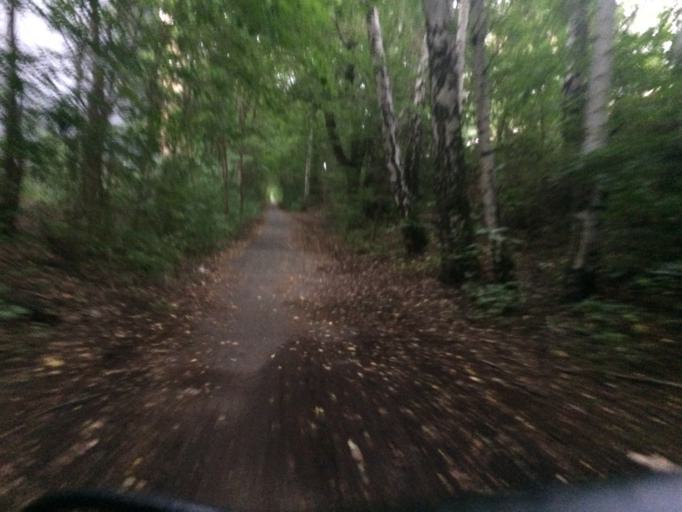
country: DE
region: Berlin
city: Markisches Viertel
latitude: 52.5869
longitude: 13.3532
